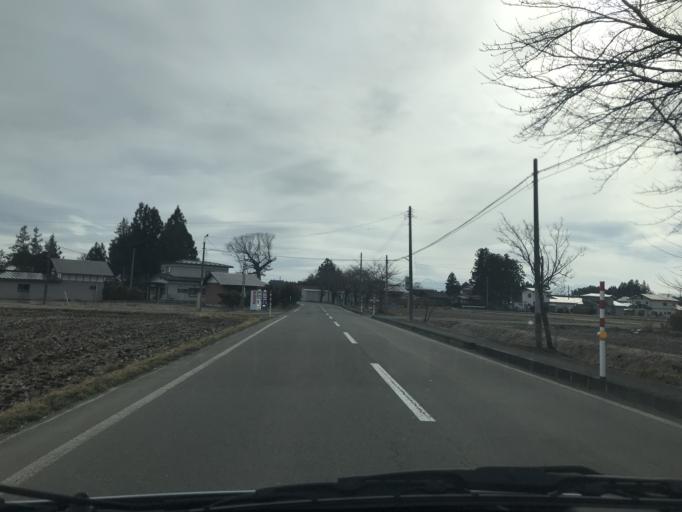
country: JP
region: Iwate
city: Hanamaki
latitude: 39.3819
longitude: 141.0719
